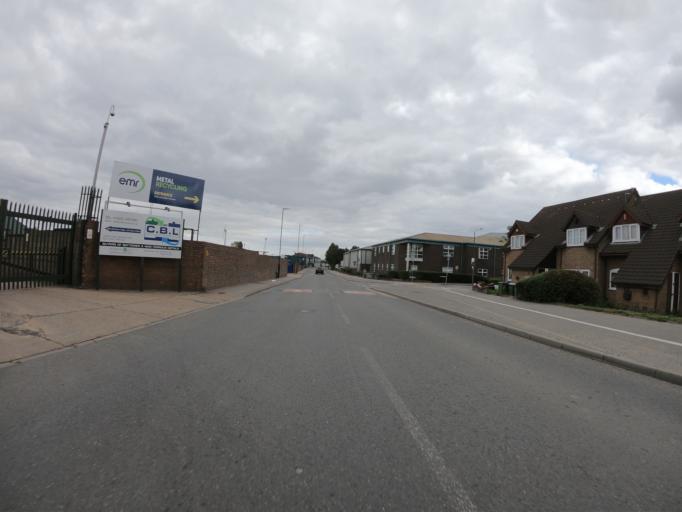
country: GB
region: England
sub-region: Greater London
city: Erith
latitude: 51.4781
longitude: 0.1877
